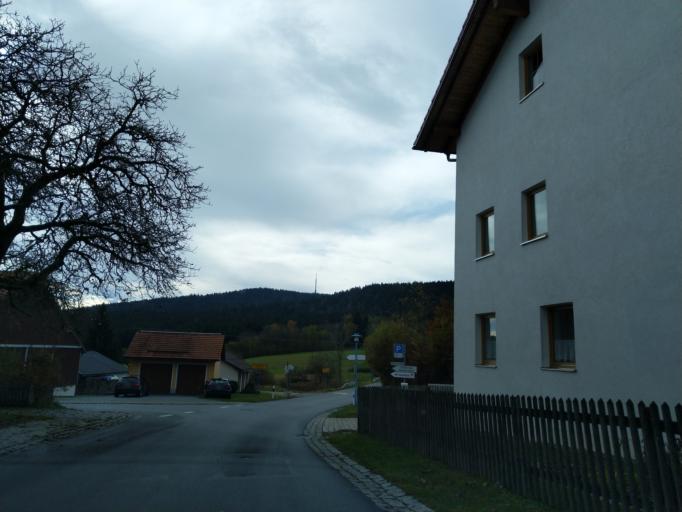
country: DE
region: Bavaria
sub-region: Lower Bavaria
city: Schofweg
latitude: 48.8383
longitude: 13.2282
